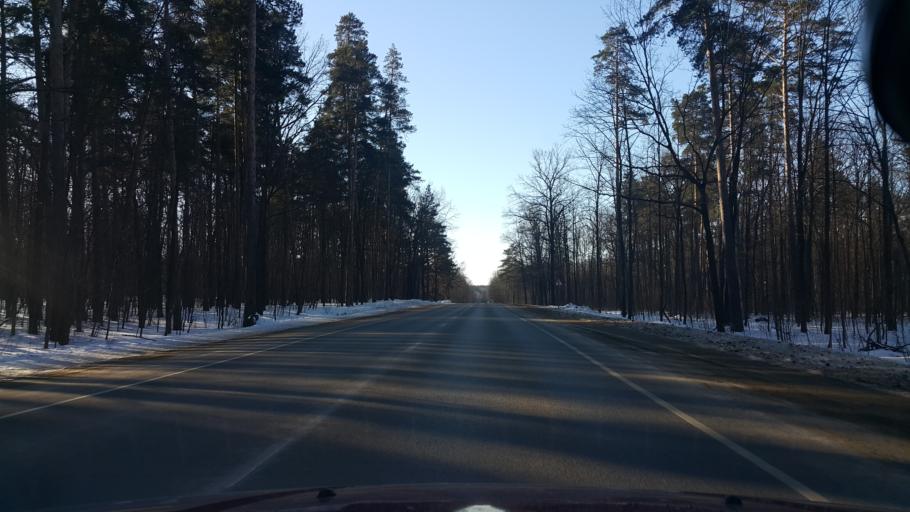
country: RU
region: Tambov
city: Novaya Lyada
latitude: 52.7014
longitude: 41.5461
